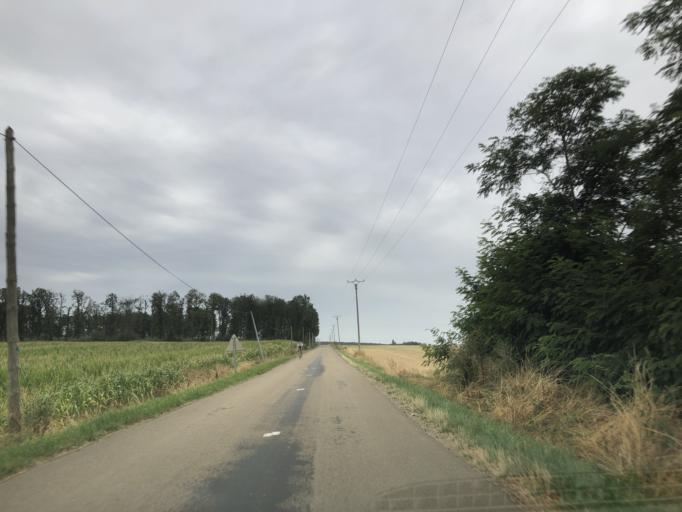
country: FR
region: Centre
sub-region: Departement du Loiret
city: Douchy
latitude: 47.9841
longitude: 3.1424
